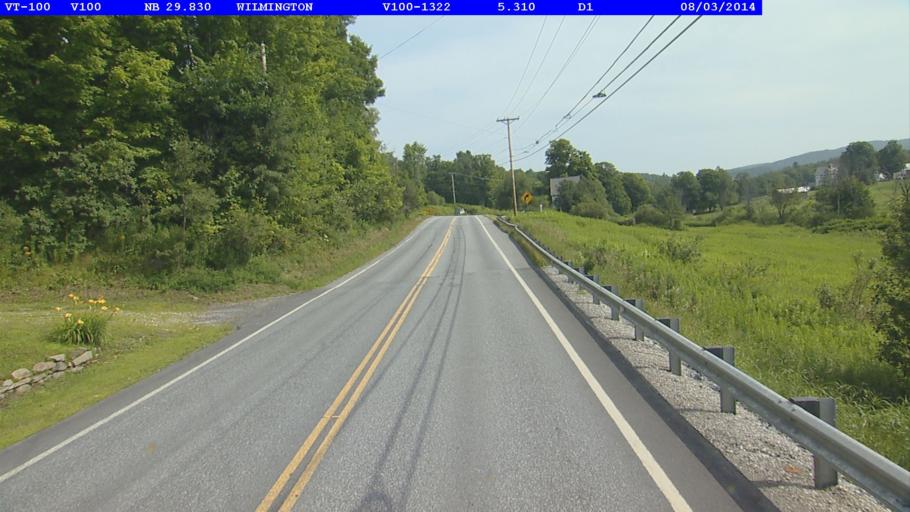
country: US
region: Vermont
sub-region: Windham County
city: Dover
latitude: 42.9028
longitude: -72.8535
